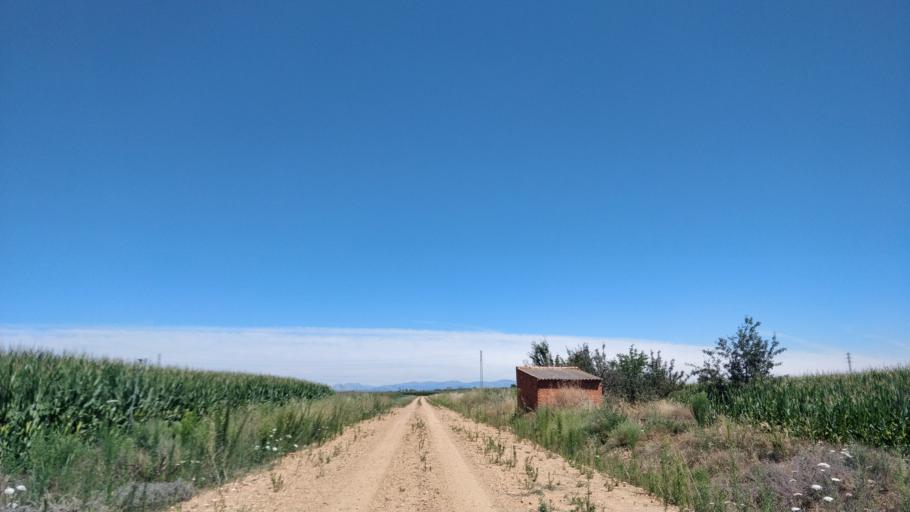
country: ES
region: Castille and Leon
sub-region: Provincia de Leon
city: Bustillo del Paramo
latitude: 42.4571
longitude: -5.8166
